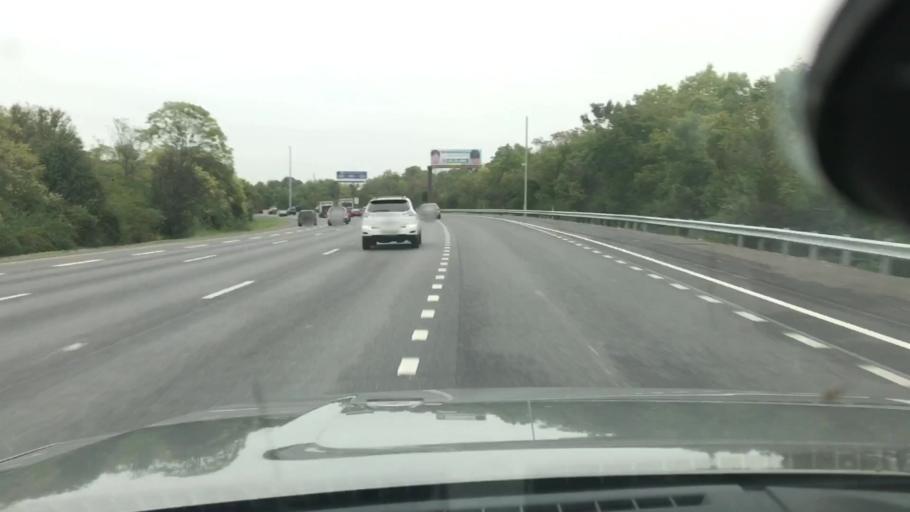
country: US
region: Tennessee
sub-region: Williamson County
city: Brentwood
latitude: 36.0457
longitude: -86.7781
